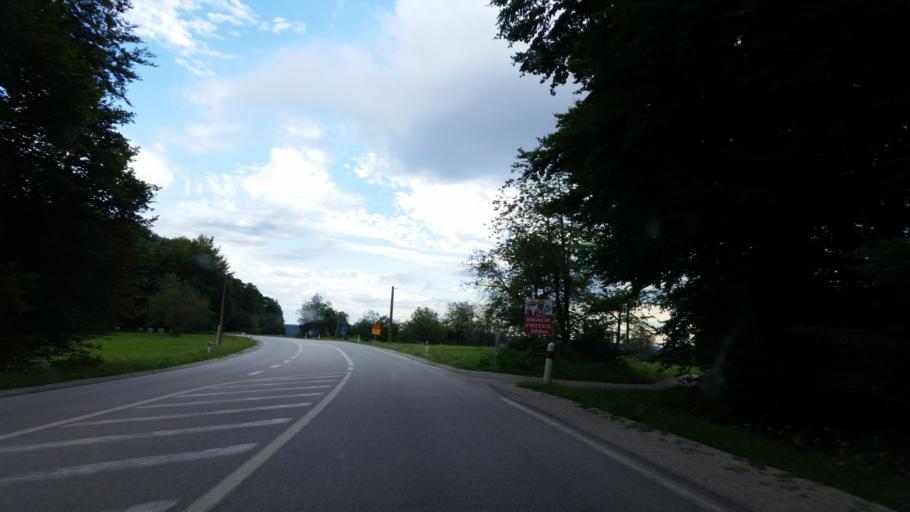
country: FR
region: Franche-Comte
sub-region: Departement de la Haute-Saone
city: Fougerolles
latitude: 47.9154
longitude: 6.4087
